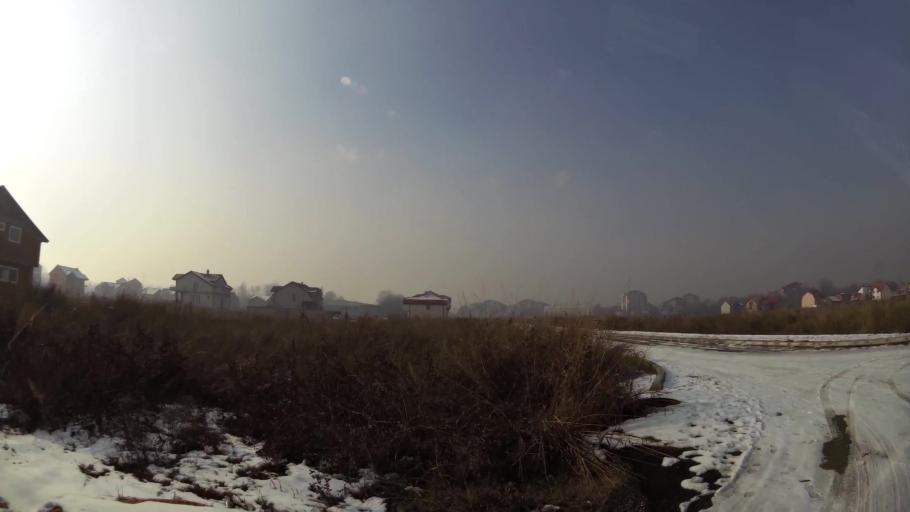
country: MK
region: Kisela Voda
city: Kisela Voda
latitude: 41.9936
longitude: 21.5172
